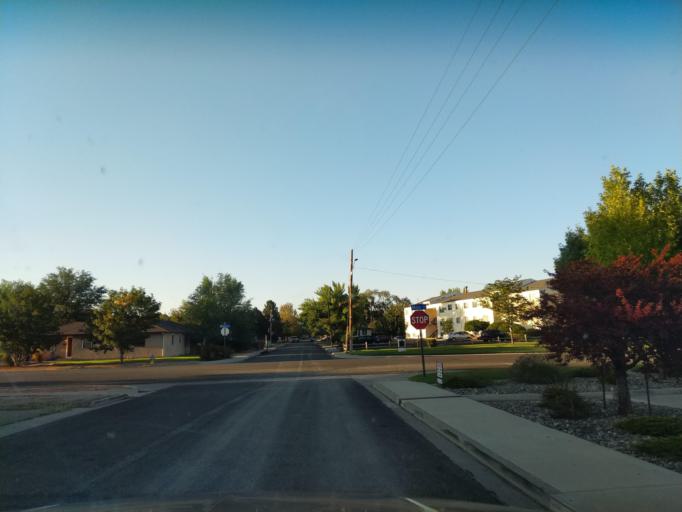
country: US
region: Colorado
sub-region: Mesa County
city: Grand Junction
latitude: 39.0670
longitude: -108.5453
